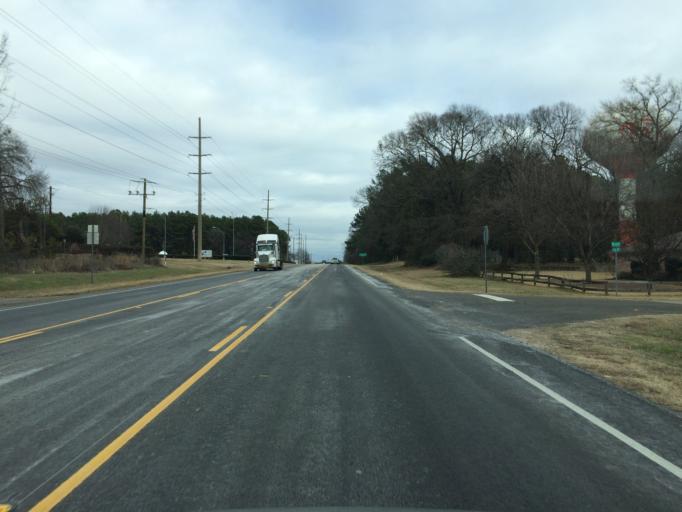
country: US
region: Texas
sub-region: Wood County
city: Mineola
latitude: 32.6881
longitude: -95.4795
